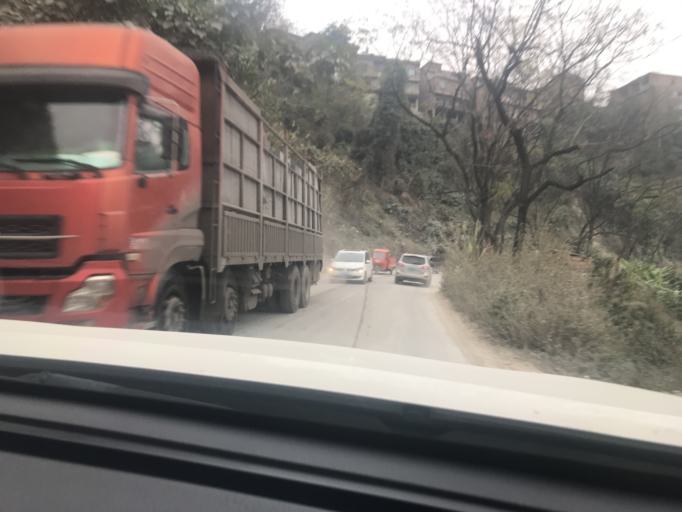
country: CN
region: Guangxi Zhuangzu Zizhiqu
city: Xinzhou
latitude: 24.9866
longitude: 105.8235
